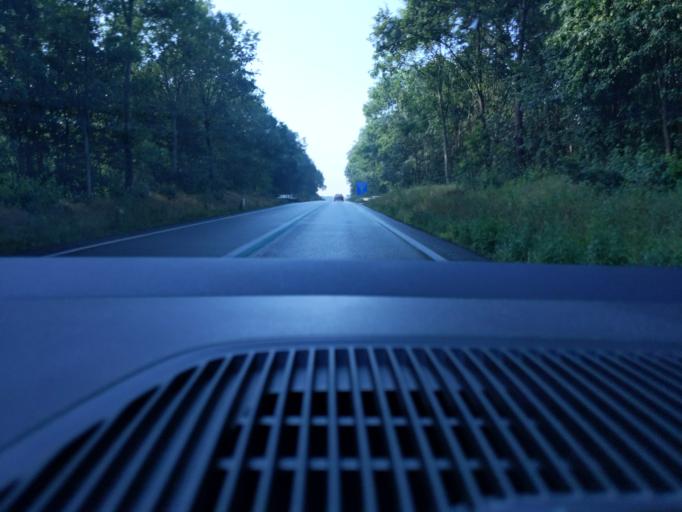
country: NL
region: Drenthe
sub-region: Gemeente Emmen
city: Emmer-Compascuum
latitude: 52.9166
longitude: 7.0373
